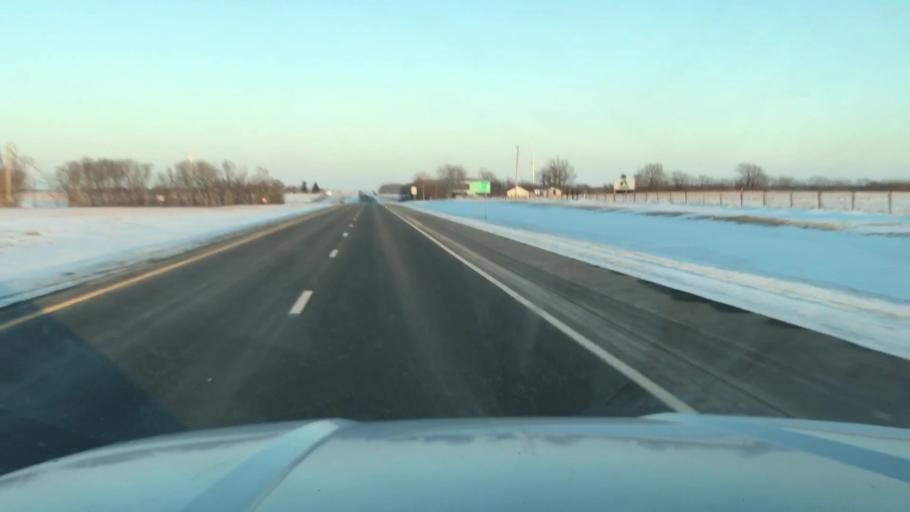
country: US
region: Missouri
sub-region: DeKalb County
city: Maysville
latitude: 39.7615
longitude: -94.4007
